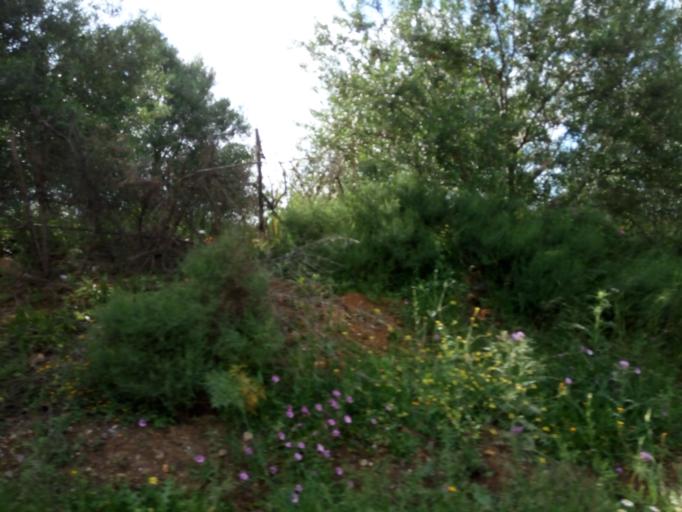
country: DZ
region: Tipaza
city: El Affroun
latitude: 36.3730
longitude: 2.5036
